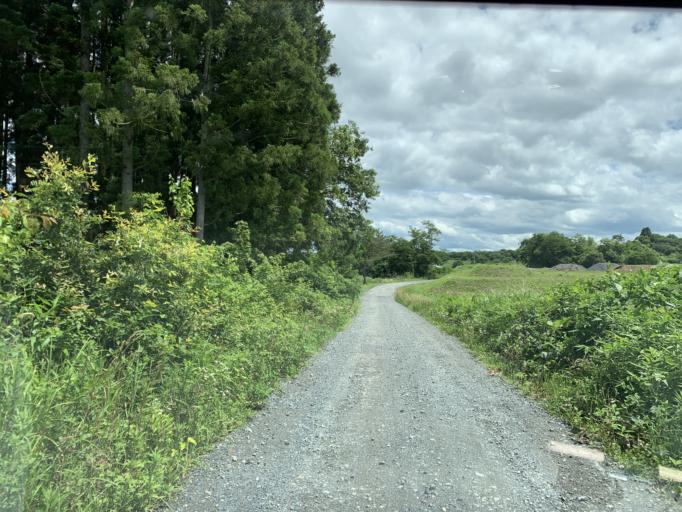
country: JP
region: Iwate
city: Ichinoseki
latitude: 38.9245
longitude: 141.0595
